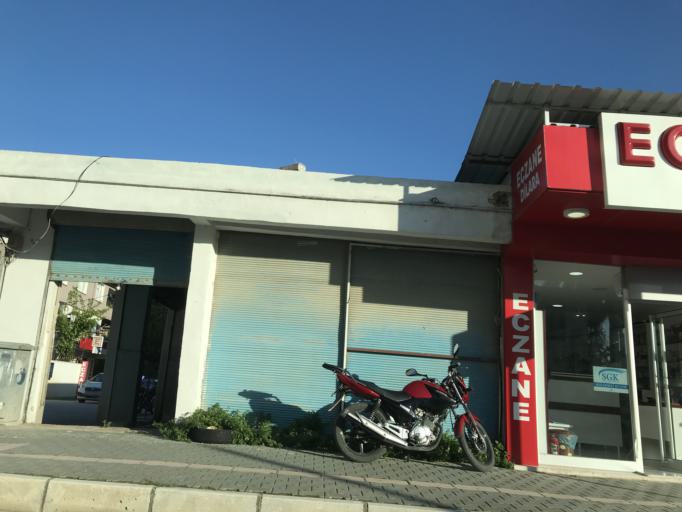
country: TR
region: Hatay
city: Samandag
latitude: 36.0822
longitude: 35.9880
